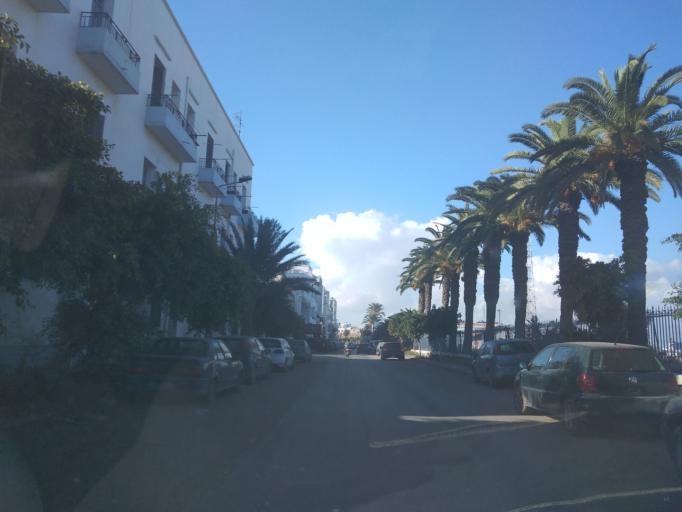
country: TN
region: Safaqis
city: Sfax
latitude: 34.7329
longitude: 10.7682
